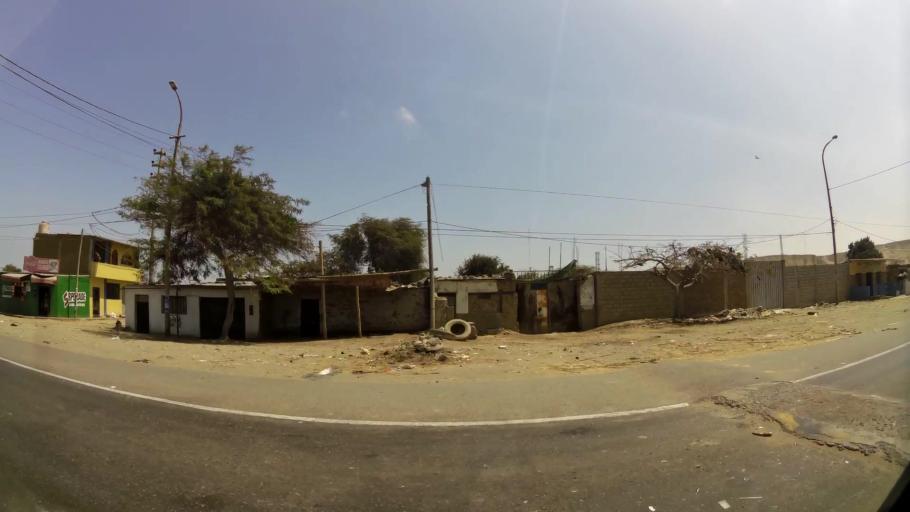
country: PE
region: La Libertad
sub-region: Provincia de Pacasmayo
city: Pacasmayo
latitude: -7.3984
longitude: -79.5581
